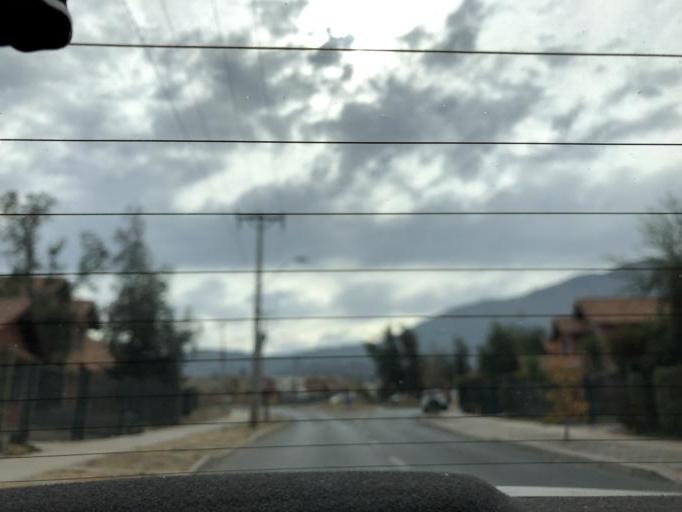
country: CL
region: Santiago Metropolitan
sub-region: Provincia de Cordillera
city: Puente Alto
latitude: -33.5844
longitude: -70.5139
